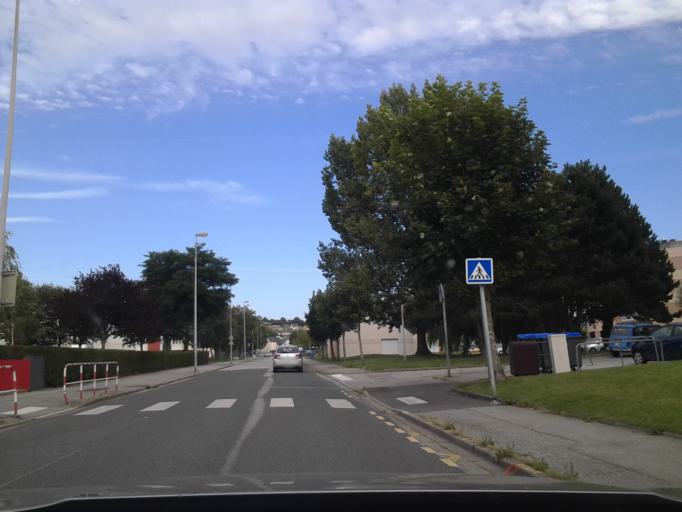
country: FR
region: Lower Normandy
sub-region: Departement de la Manche
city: Tourlaville
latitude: 49.6439
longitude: -1.5790
